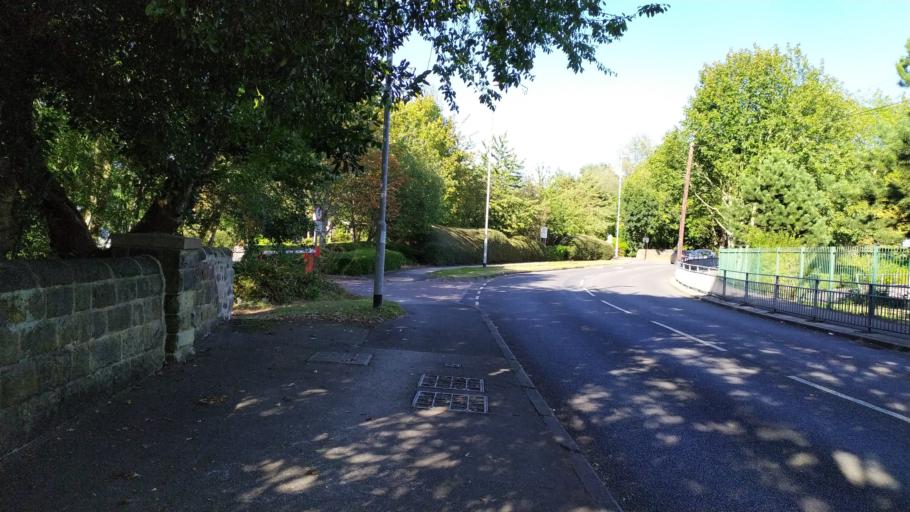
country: GB
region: England
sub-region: City and Borough of Leeds
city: Chapel Allerton
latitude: 53.8395
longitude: -1.5616
